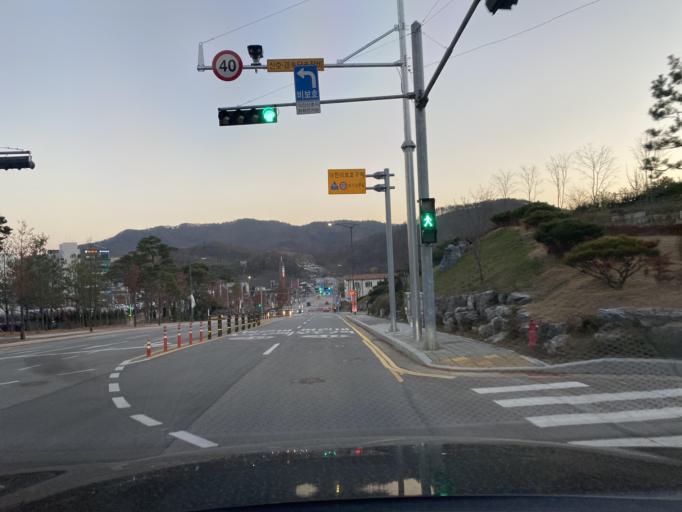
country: KR
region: Chungcheongnam-do
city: Yesan
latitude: 36.6816
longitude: 126.8434
